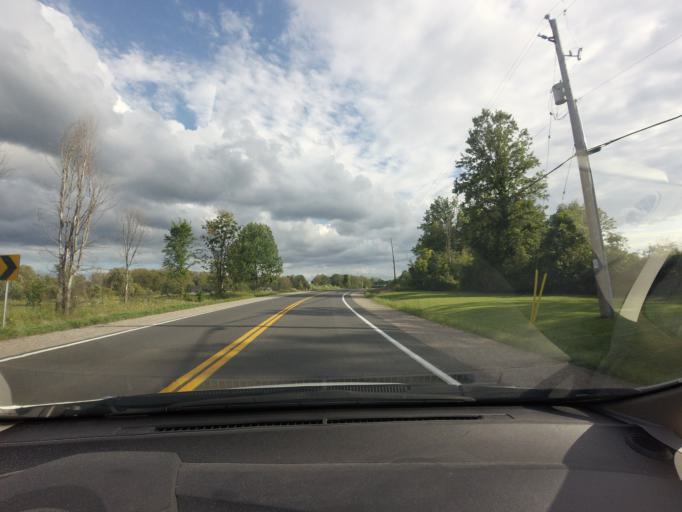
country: CA
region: Ontario
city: Perth
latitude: 44.8187
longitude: -76.3171
